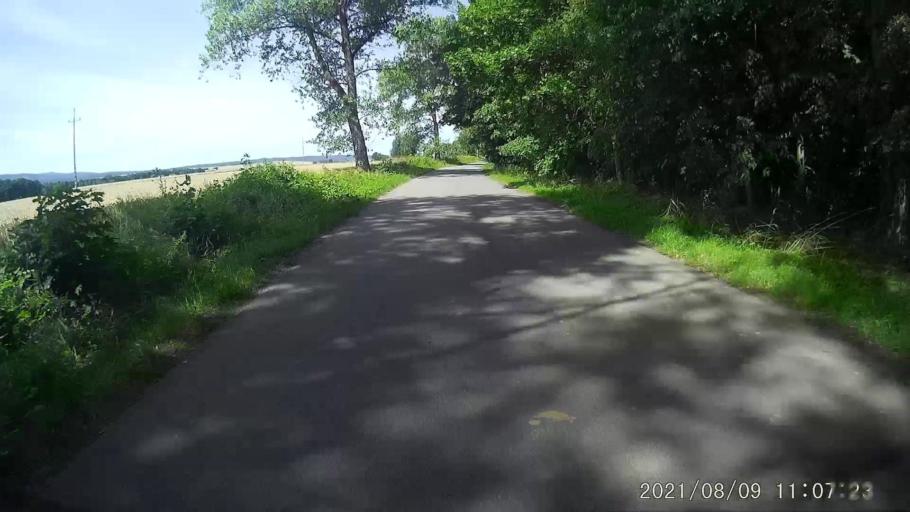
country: PL
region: Lower Silesian Voivodeship
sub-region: Powiat klodzki
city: Bozkow
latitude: 50.4559
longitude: 16.5982
